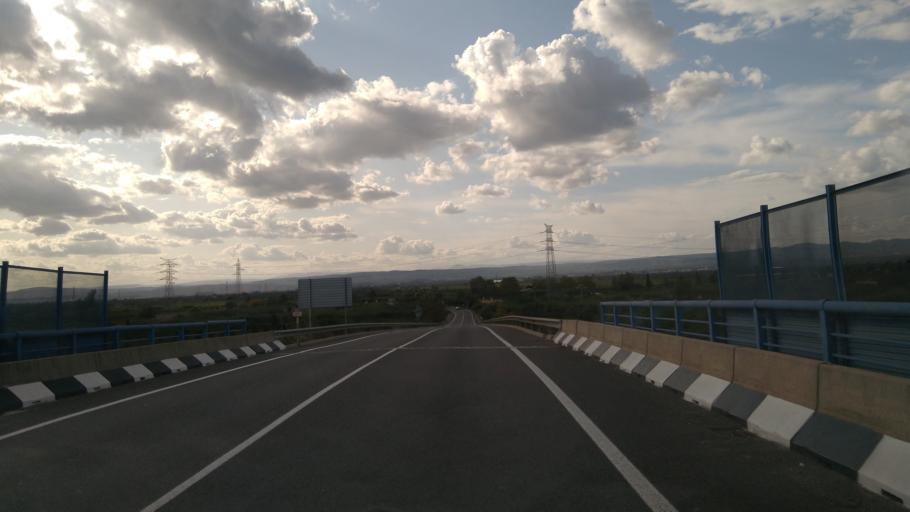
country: ES
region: Valencia
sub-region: Provincia de Valencia
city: Alzira
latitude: 39.1635
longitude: -0.4490
